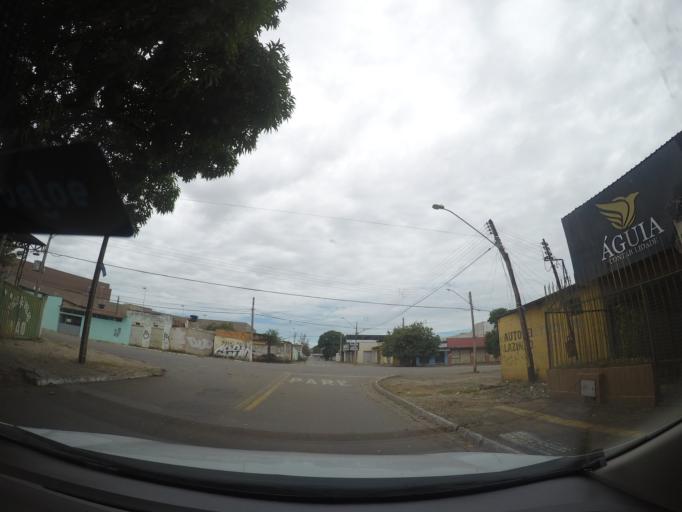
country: BR
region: Goias
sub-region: Goiania
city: Goiania
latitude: -16.6646
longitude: -49.3097
